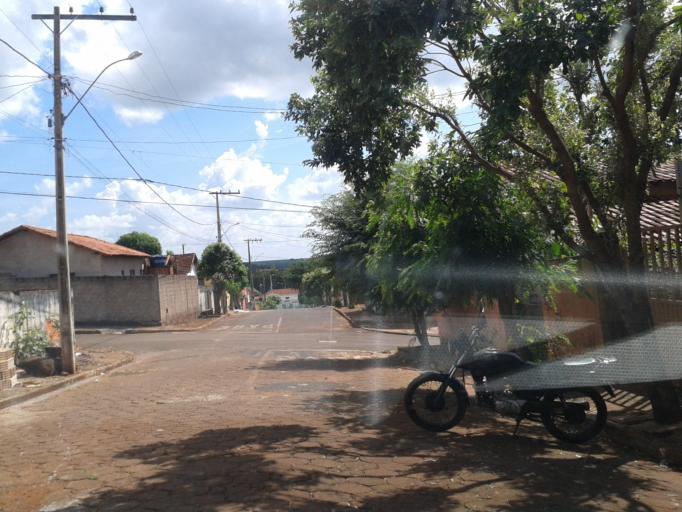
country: BR
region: Minas Gerais
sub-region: Capinopolis
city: Capinopolis
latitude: -18.6842
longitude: -49.5765
